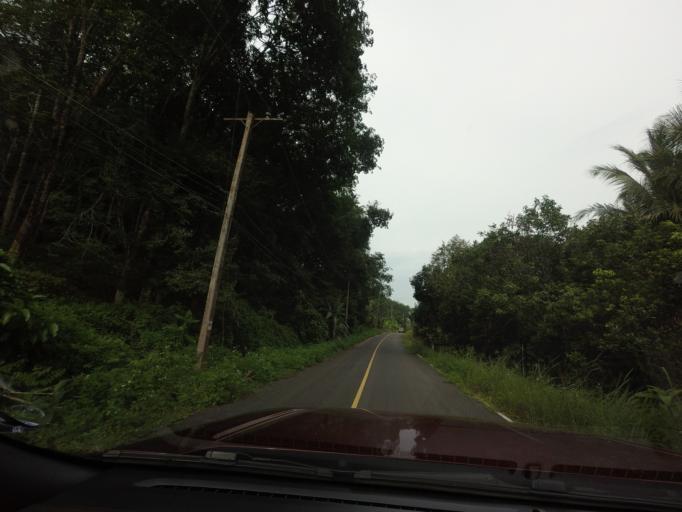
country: TH
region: Narathiwat
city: Si Sakhon
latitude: 6.0620
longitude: 101.3893
